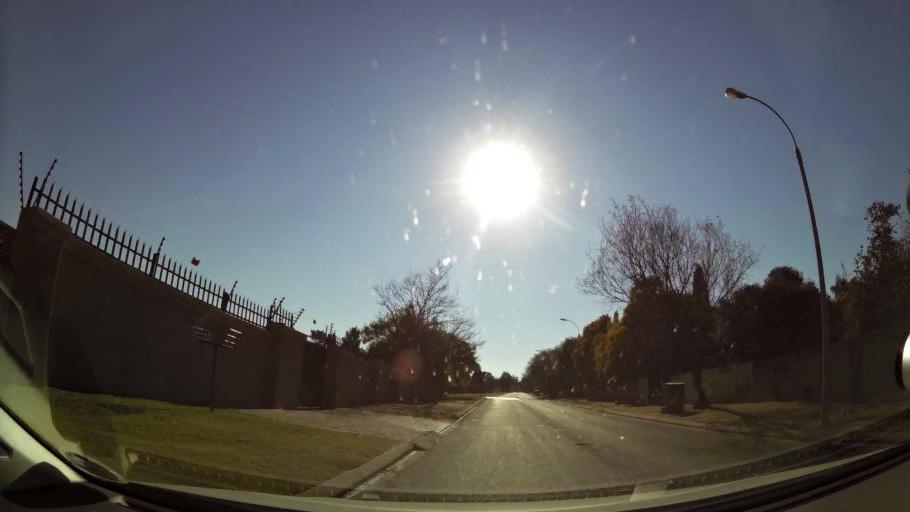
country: ZA
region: Gauteng
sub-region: City of Johannesburg Metropolitan Municipality
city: Modderfontein
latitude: -26.0602
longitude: 28.1976
